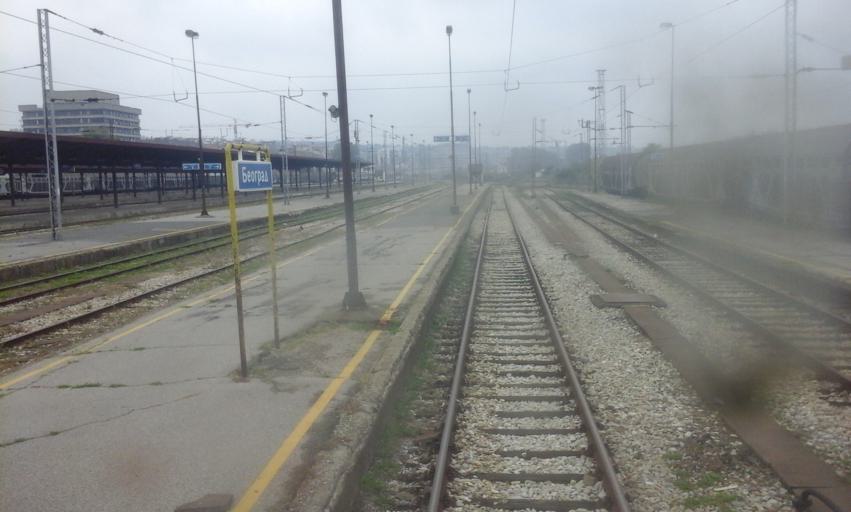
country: RS
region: Central Serbia
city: Belgrade
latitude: 44.8082
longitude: 20.4543
